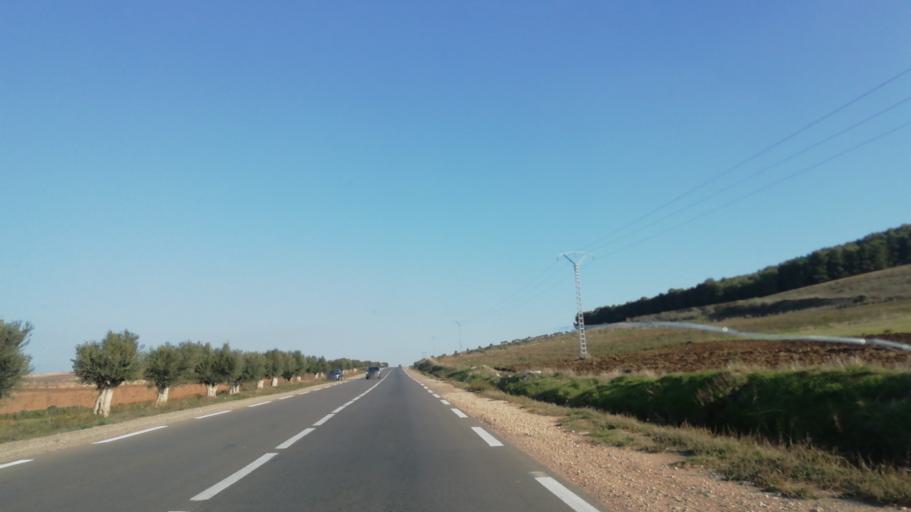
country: DZ
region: Ain Temouchent
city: Hammam Bou Hadjar
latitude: 35.1654
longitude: -0.8827
